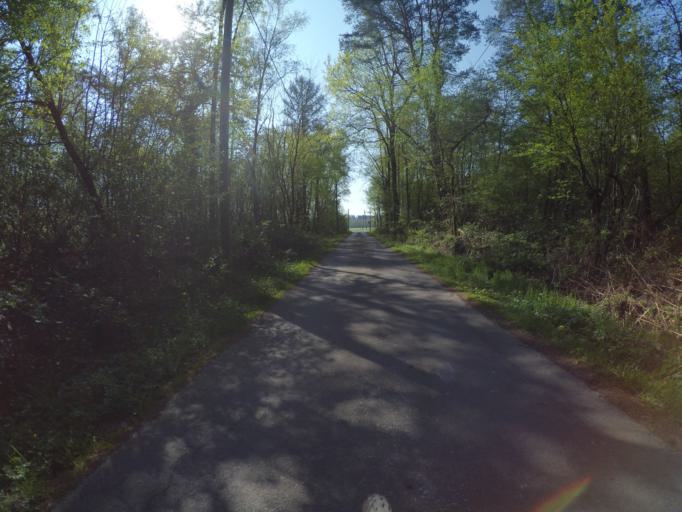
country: DE
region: North Rhine-Westphalia
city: Ludinghausen
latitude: 51.7999
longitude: 7.4291
